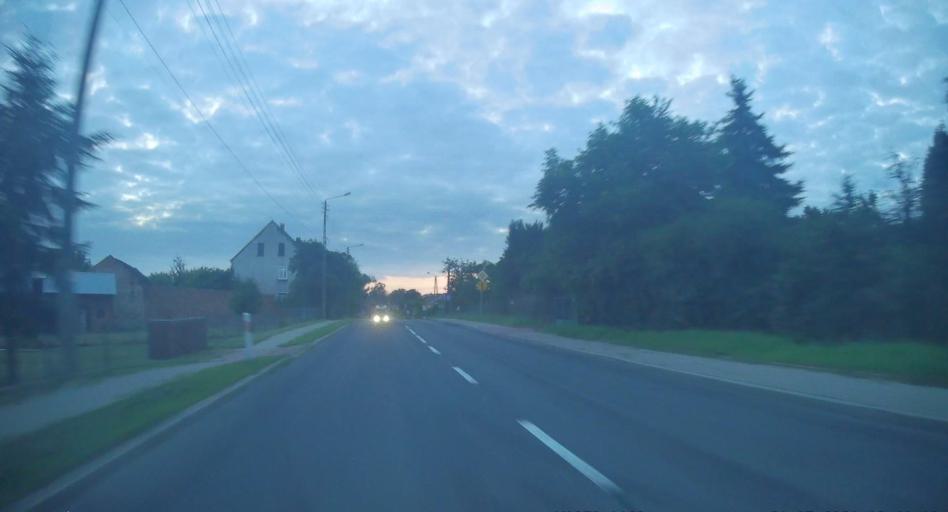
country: PL
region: Opole Voivodeship
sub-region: Powiat oleski
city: Dalachow
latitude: 51.0364
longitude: 18.6067
